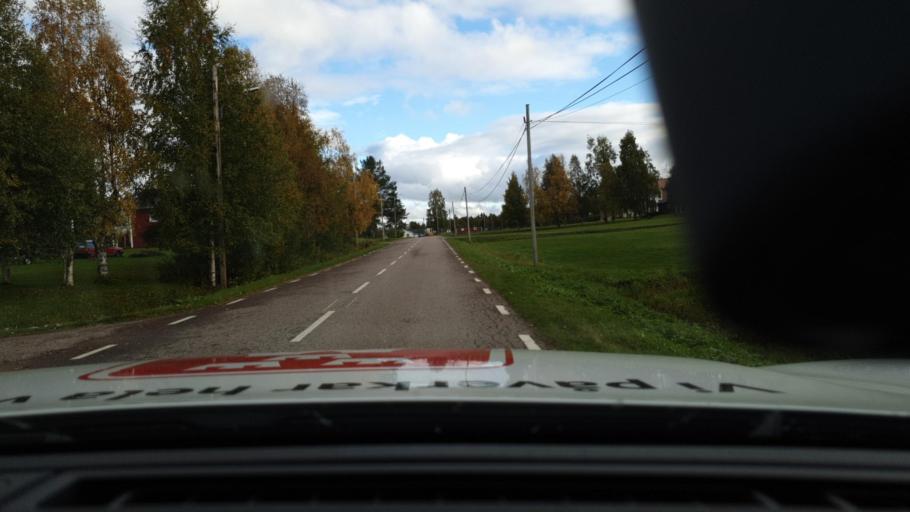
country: SE
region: Norrbotten
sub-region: Overkalix Kommun
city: OEverkalix
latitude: 67.0049
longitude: 22.4912
